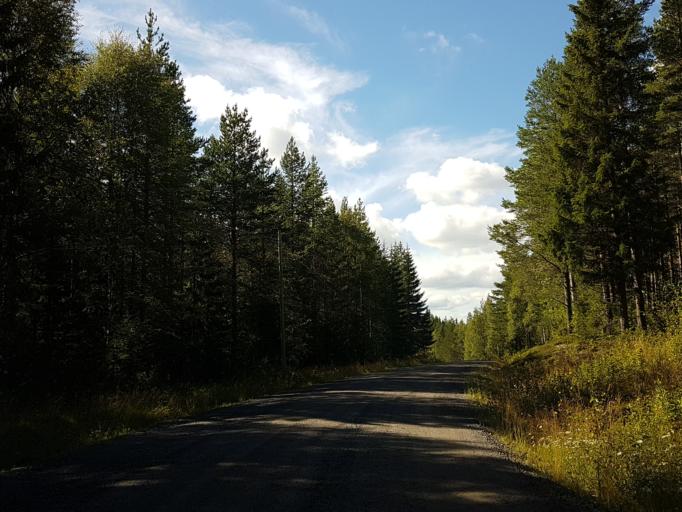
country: SE
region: Vaesterbotten
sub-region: Skelleftea Kommun
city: Burtraesk
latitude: 64.2788
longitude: 20.4765
